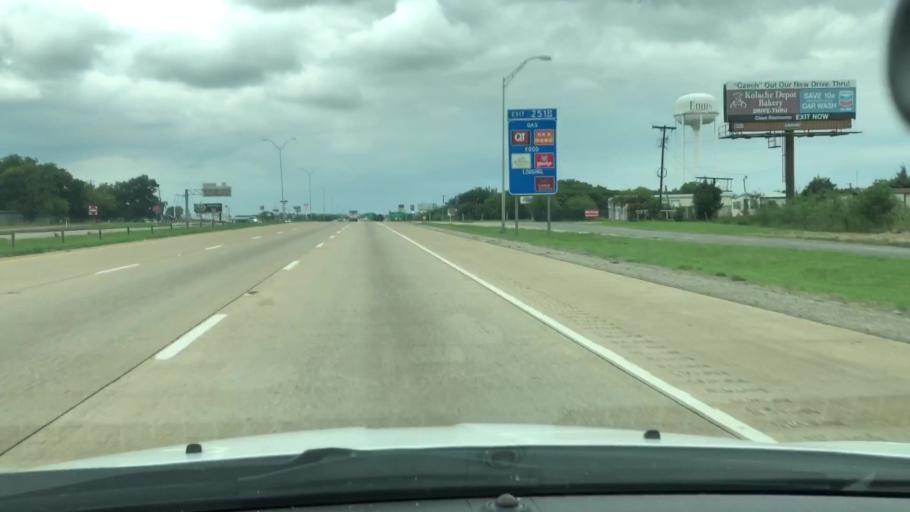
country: US
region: Texas
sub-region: Ellis County
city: Ennis
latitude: 32.3262
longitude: -96.6098
